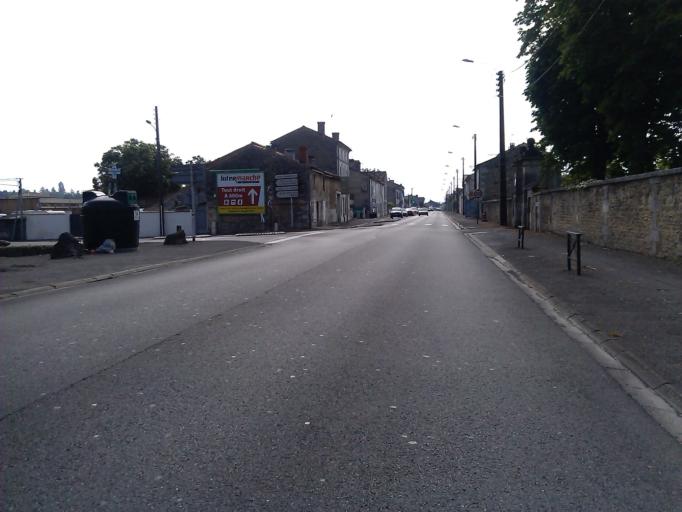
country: FR
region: Poitou-Charentes
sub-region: Departement de la Charente
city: Angouleme
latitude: 45.6629
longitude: 0.1315
